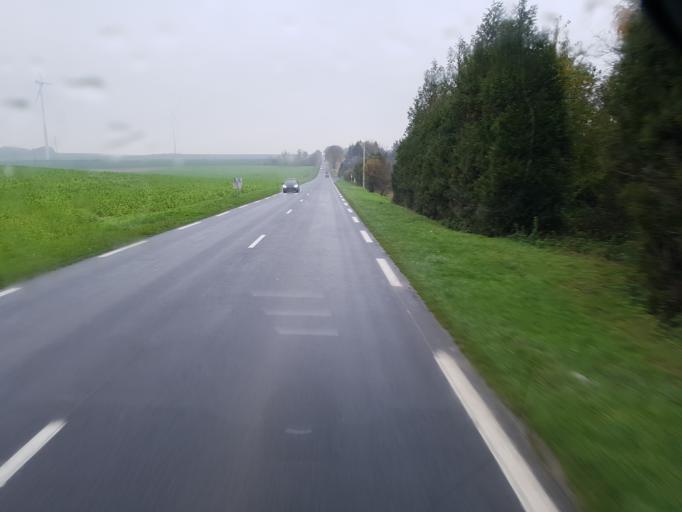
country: FR
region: Picardie
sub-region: Departement de l'Aisne
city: Saint-Quentin
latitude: 49.8920
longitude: 3.2647
